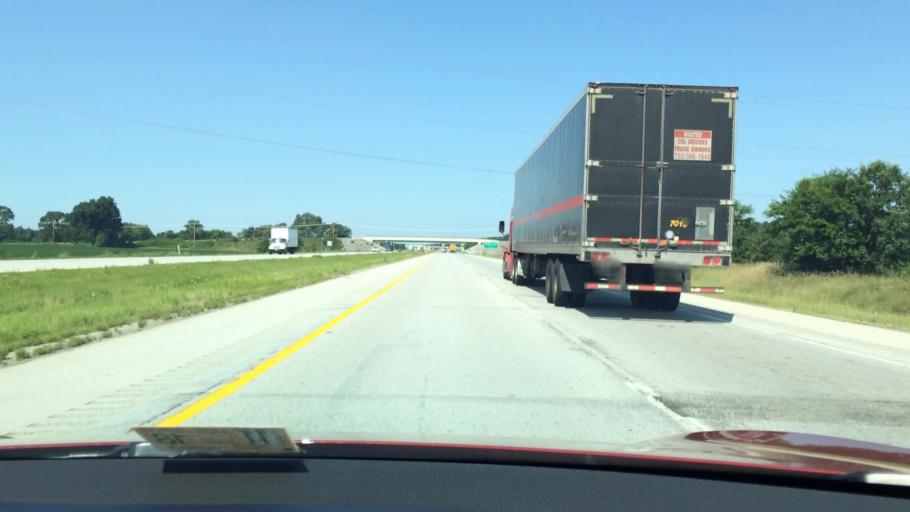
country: US
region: Indiana
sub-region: Elkhart County
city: Bristol
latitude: 41.7312
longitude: -85.8653
